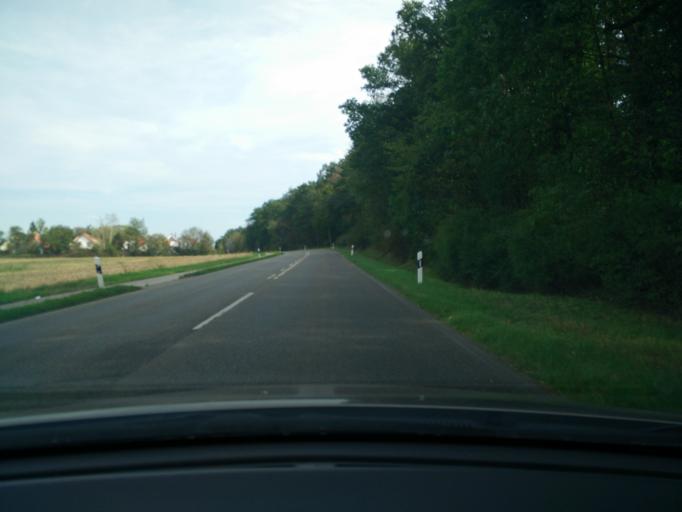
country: DE
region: Bavaria
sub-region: Regierungsbezirk Mittelfranken
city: Seukendorf
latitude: 49.4882
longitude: 10.9035
